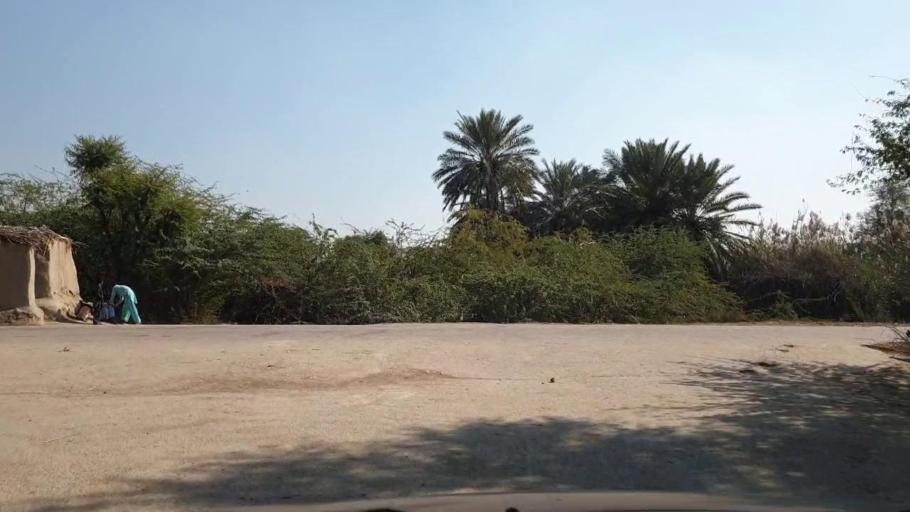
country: PK
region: Sindh
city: Jhol
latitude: 25.9098
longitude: 68.8069
